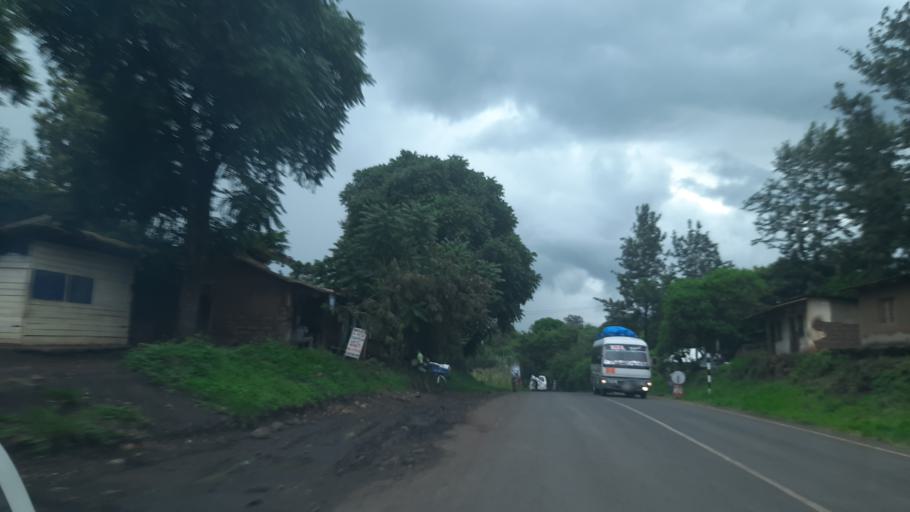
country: TZ
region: Arusha
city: Usa River
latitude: -3.3978
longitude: 36.8074
